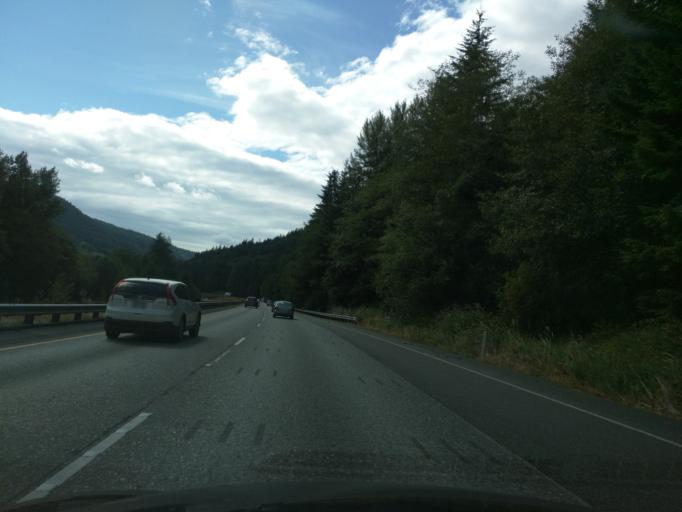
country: US
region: Washington
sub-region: Whatcom County
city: Geneva
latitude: 48.6902
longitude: -122.4078
